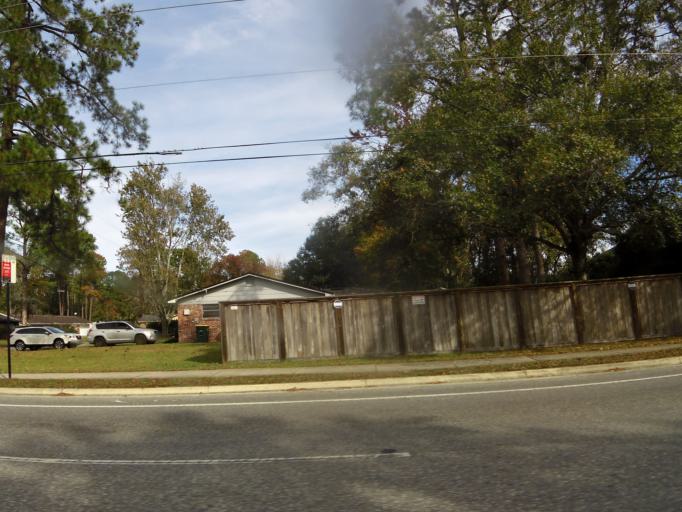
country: US
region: Florida
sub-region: Saint Johns County
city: Fruit Cove
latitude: 30.2241
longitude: -81.5933
